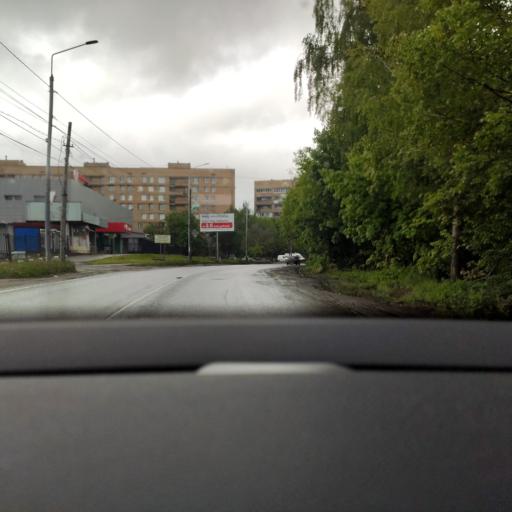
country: RU
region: Moskovskaya
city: Saltykovka
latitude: 55.7342
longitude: 37.9682
